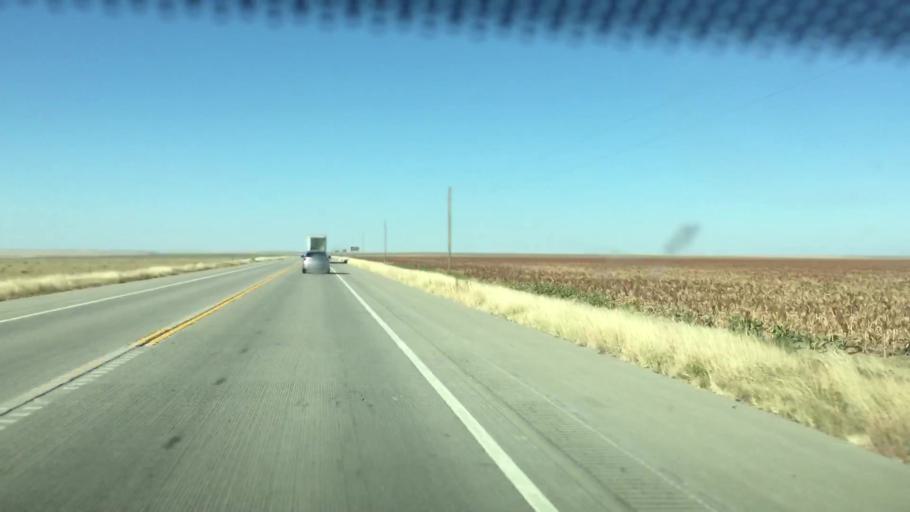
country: US
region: Colorado
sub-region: Kiowa County
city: Eads
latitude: 38.2906
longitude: -102.7199
